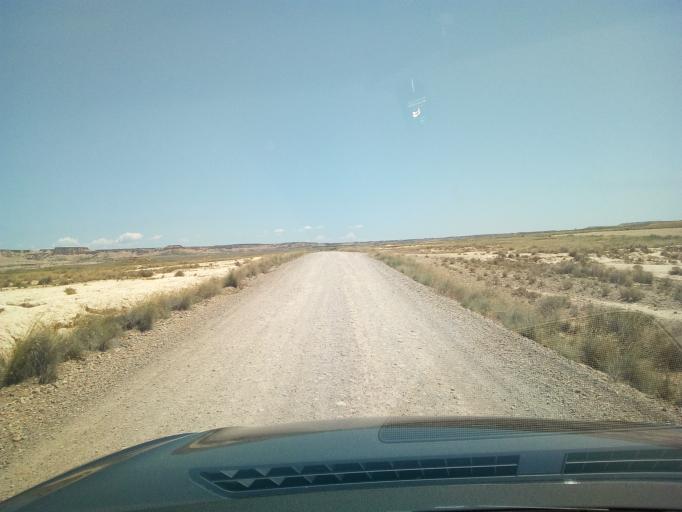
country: ES
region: Navarre
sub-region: Provincia de Navarra
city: Arguedas
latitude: 42.1815
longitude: -1.4629
